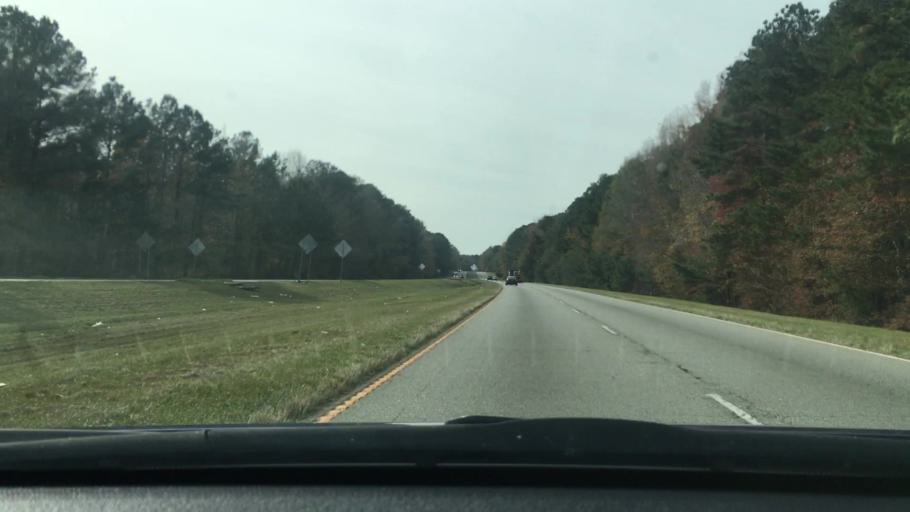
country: US
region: South Carolina
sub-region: Sumter County
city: Stateburg
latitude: 33.9466
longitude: -80.6357
